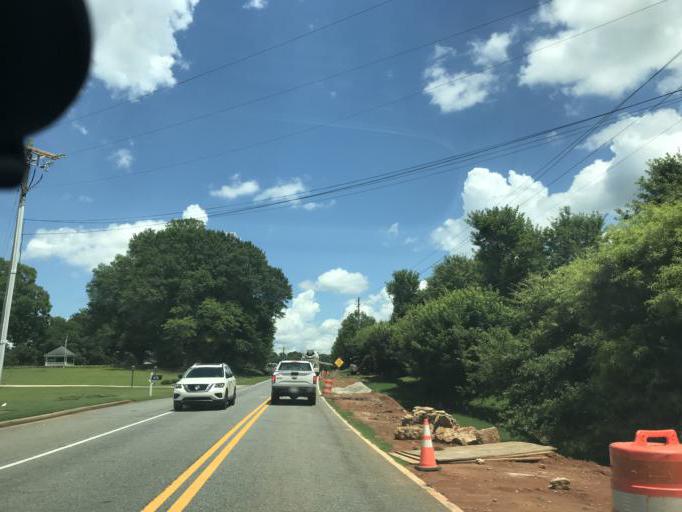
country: US
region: Georgia
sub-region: Forsyth County
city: Cumming
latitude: 34.1736
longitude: -84.1226
